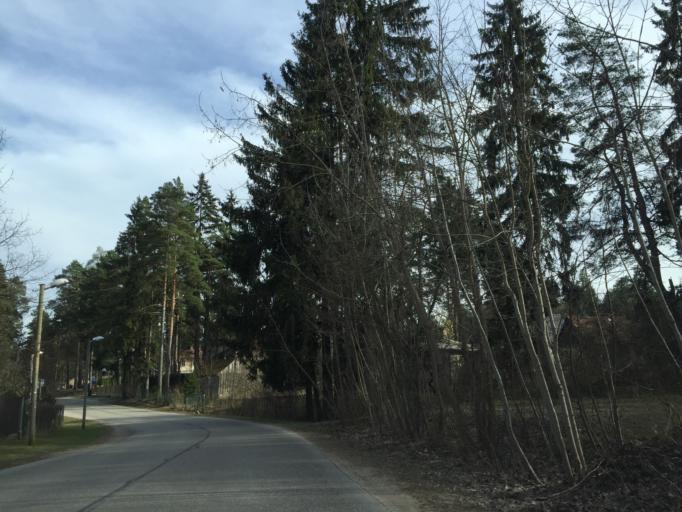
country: LV
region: Ogre
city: Ogre
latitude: 56.8115
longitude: 24.6274
